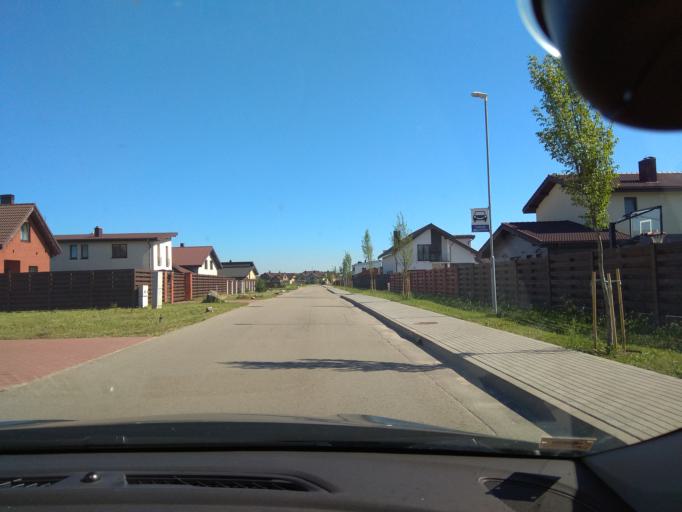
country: LT
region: Klaipedos apskritis
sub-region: Klaipeda
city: Klaipeda
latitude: 55.7515
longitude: 21.1769
